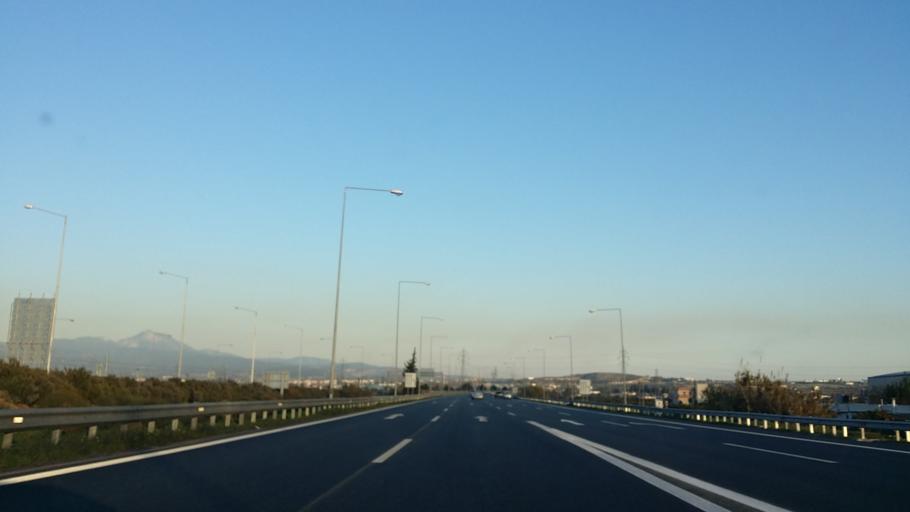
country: GR
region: Peloponnese
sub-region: Nomos Korinthias
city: Examilia
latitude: 37.9187
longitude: 22.9119
